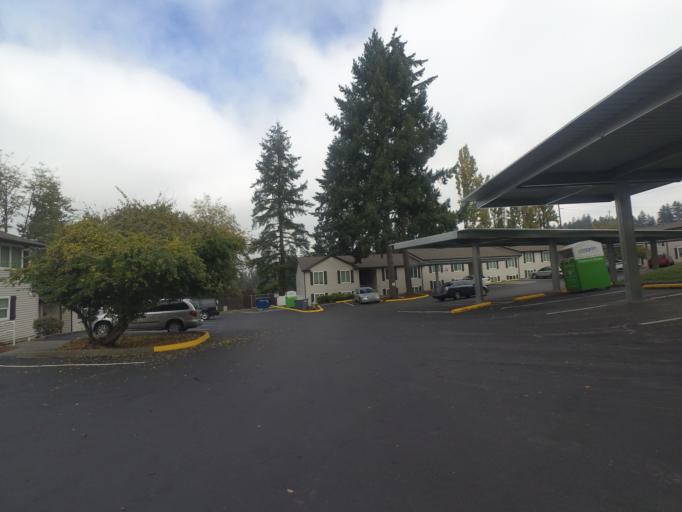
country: US
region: Washington
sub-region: Pierce County
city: Fircrest
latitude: 47.2059
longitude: -122.5079
